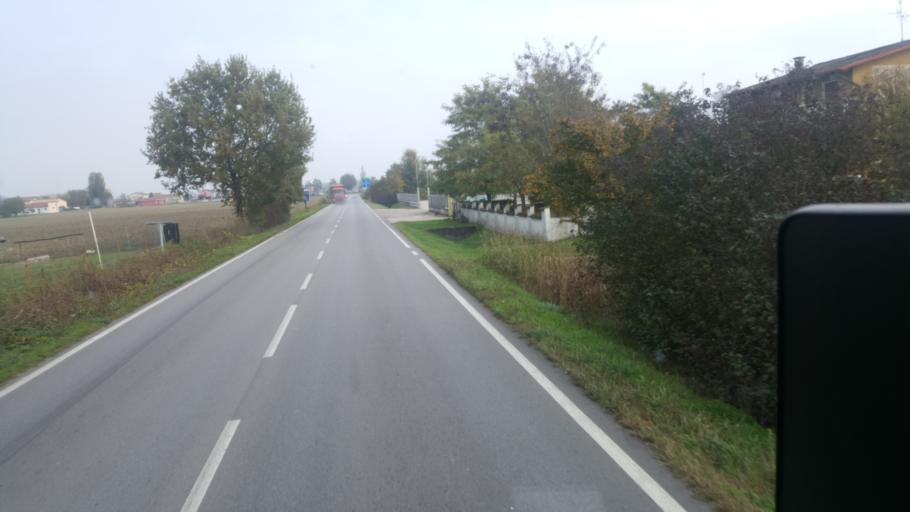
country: IT
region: Lombardy
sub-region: Provincia di Mantova
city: Palidano
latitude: 44.9855
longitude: 10.7967
